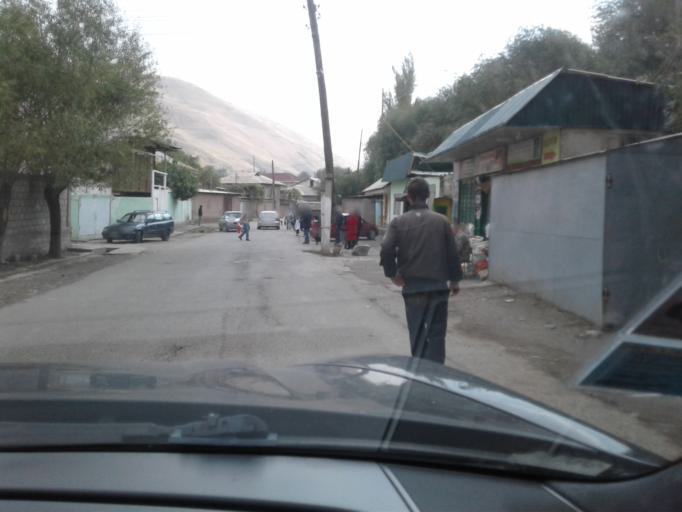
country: TJ
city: Shahrinav
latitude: 38.6193
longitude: 68.3293
